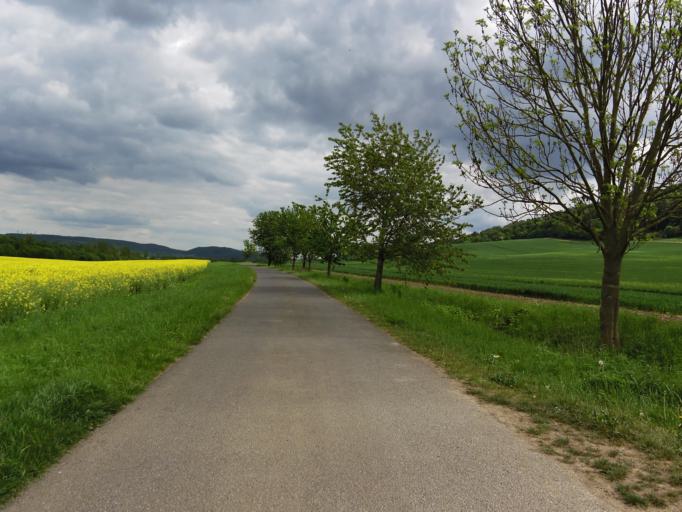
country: DE
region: Thuringia
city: Ifta
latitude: 51.0561
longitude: 10.1859
